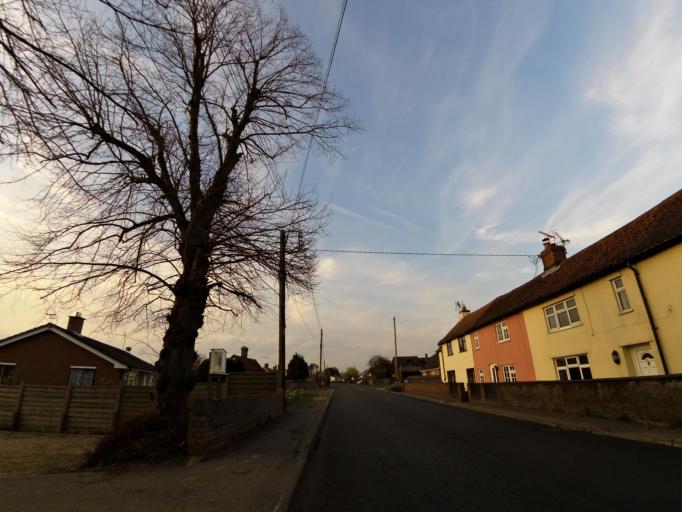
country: GB
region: England
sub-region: Suffolk
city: Ipswich
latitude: 52.1211
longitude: 1.1885
